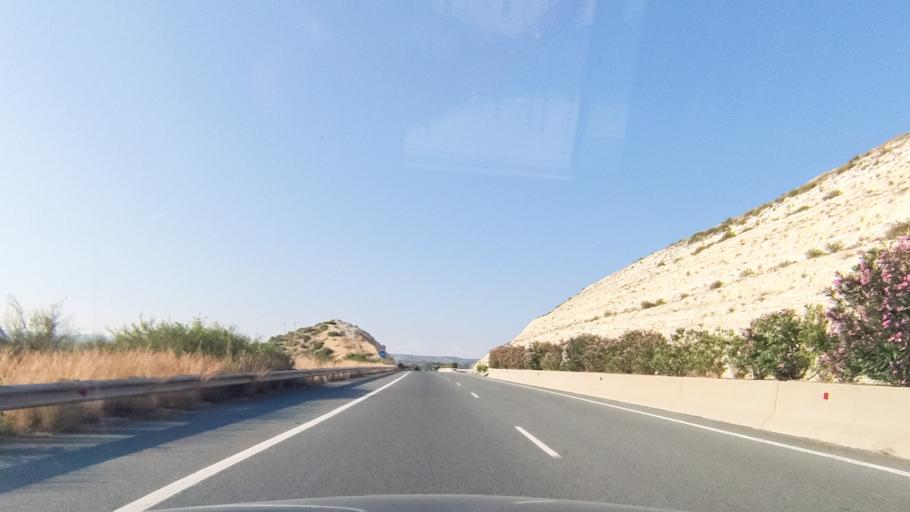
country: CY
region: Limassol
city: Sotira
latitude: 34.6824
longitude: 32.8054
